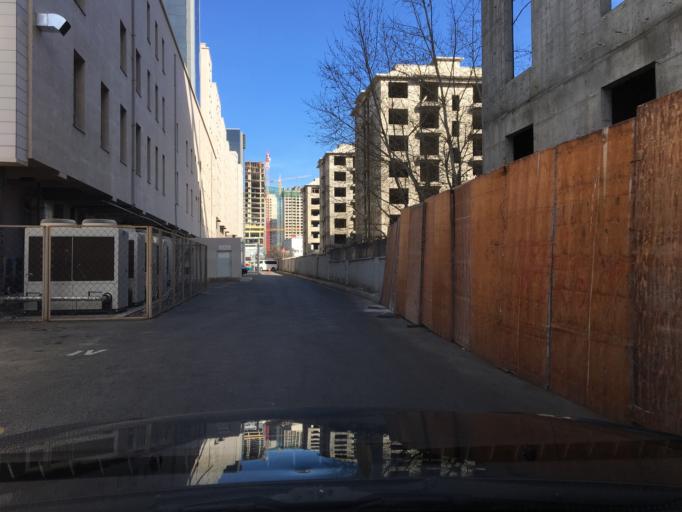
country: MN
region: Ulaanbaatar
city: Ulaanbaatar
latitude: 47.8966
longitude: 106.9089
